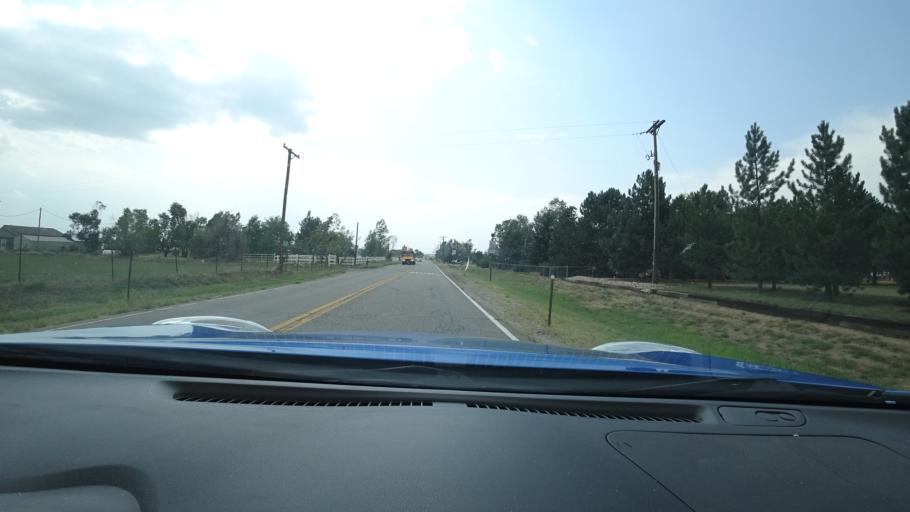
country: US
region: Colorado
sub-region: Adams County
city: Todd Creek
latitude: 39.9216
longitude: -104.8415
